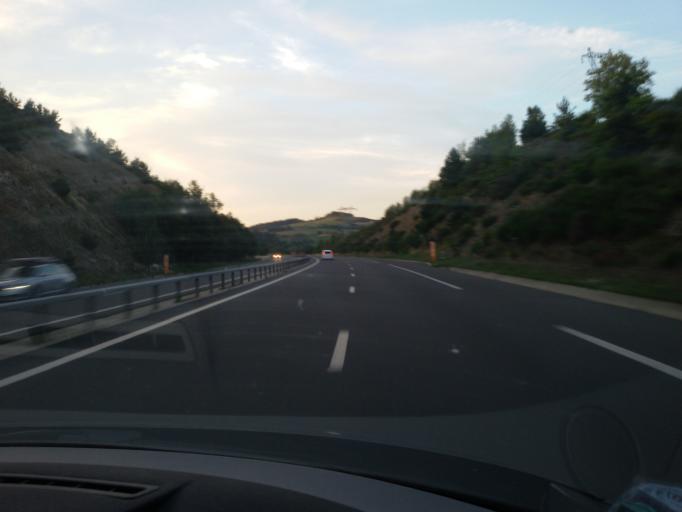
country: FR
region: Languedoc-Roussillon
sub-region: Departement de la Lozere
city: Marvejols
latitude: 44.6094
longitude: 3.2582
